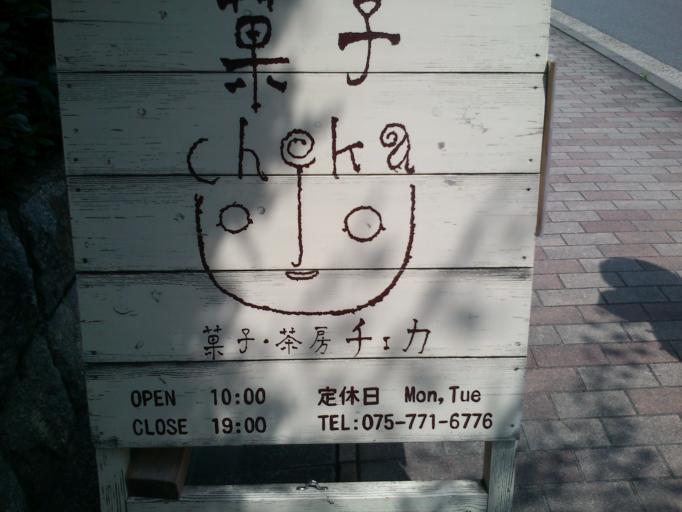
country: JP
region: Kyoto
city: Kyoto
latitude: 35.0136
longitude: 135.7872
